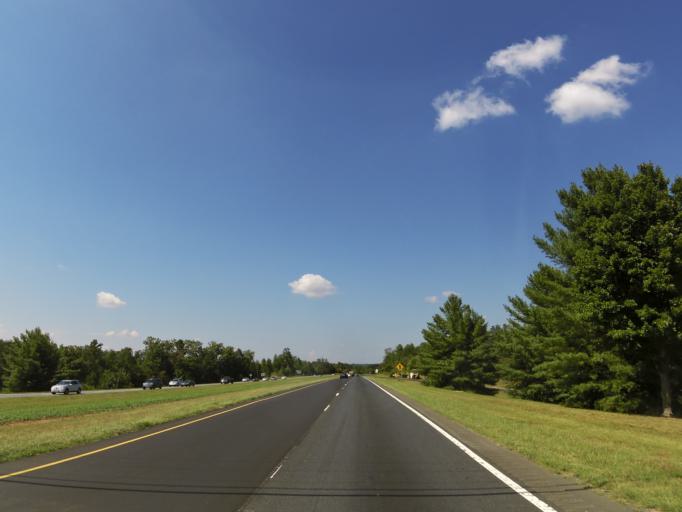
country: US
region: North Carolina
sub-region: Lincoln County
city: Lincolnton
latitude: 35.4159
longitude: -81.2107
